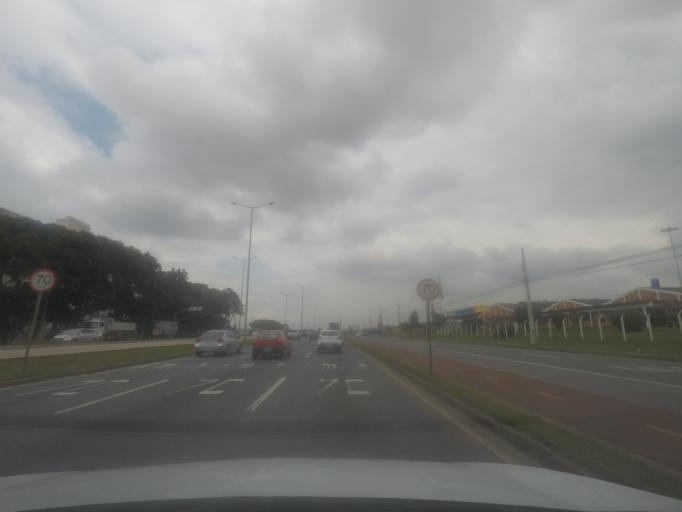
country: BR
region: Parana
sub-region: Sao Jose Dos Pinhais
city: Sao Jose dos Pinhais
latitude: -25.5132
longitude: -49.2895
